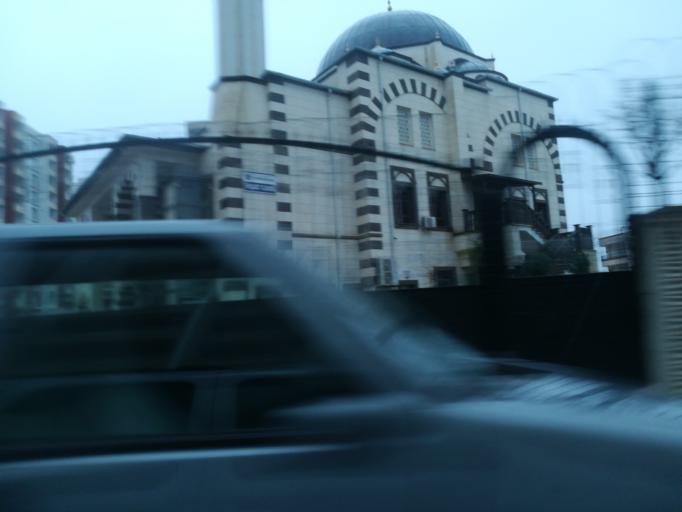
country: TR
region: Adana
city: Seyhan
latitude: 37.0076
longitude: 35.2770
